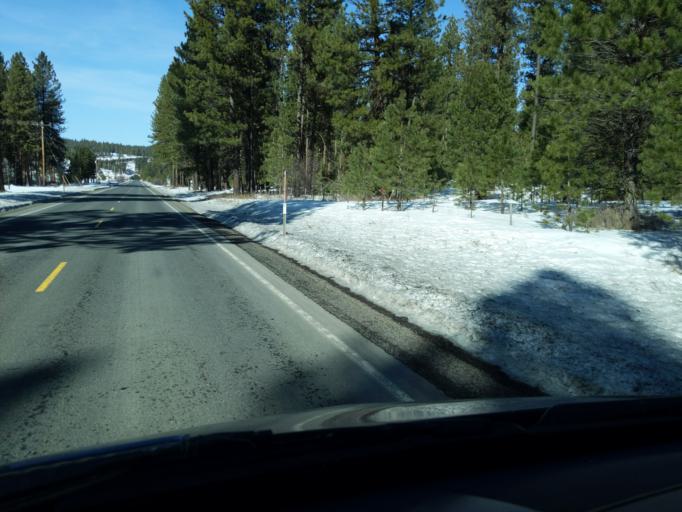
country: US
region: Oregon
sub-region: Grant County
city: John Day
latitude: 44.9232
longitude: -119.0099
